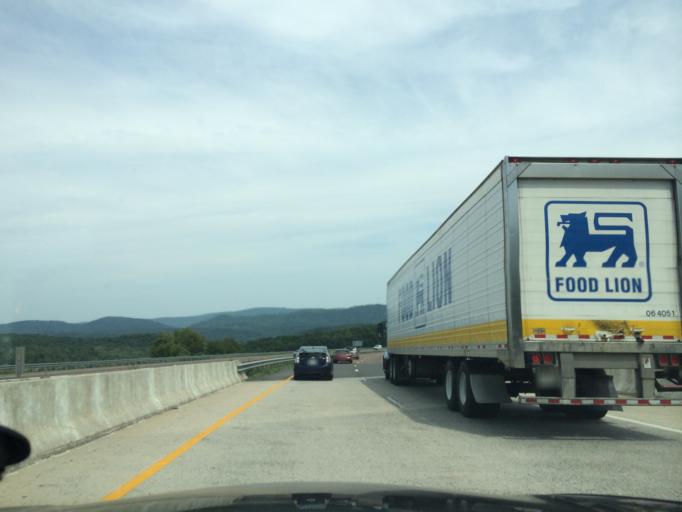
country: US
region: Maryland
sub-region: Allegany County
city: Cumberland
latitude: 39.7143
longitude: -78.6111
